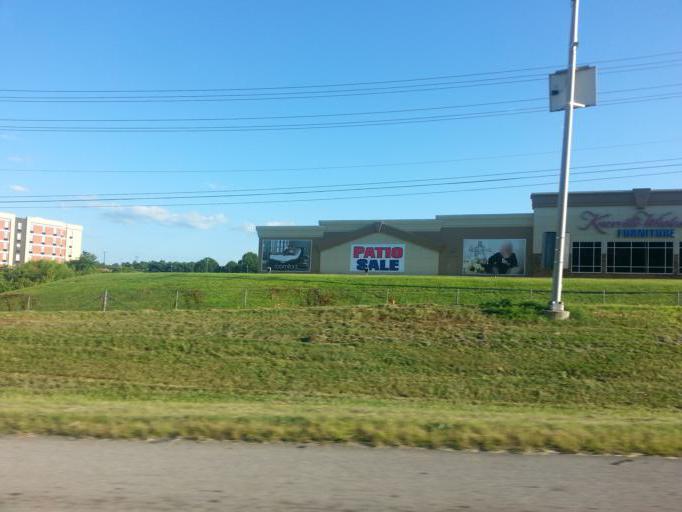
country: US
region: Tennessee
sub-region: Knox County
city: Farragut
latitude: 35.9162
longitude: -84.0983
